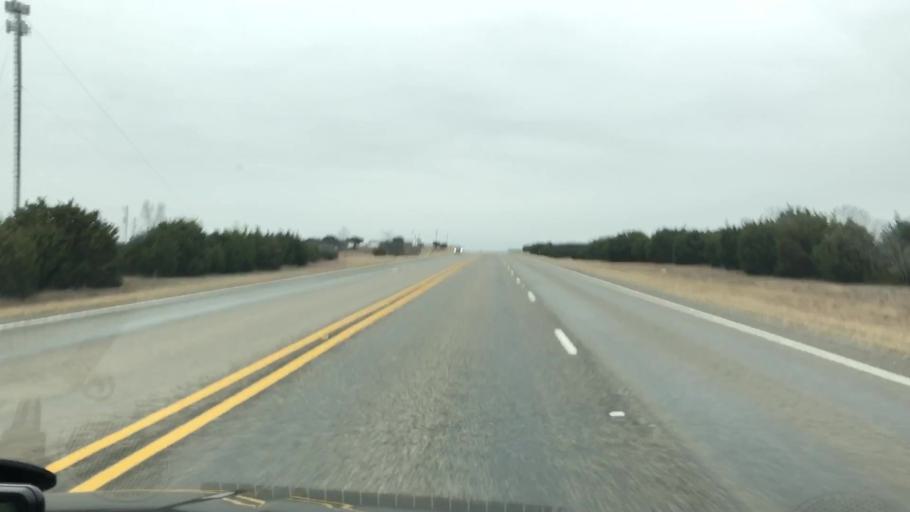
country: US
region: Texas
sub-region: Lampasas County
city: Lampasas
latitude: 31.1800
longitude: -98.1732
